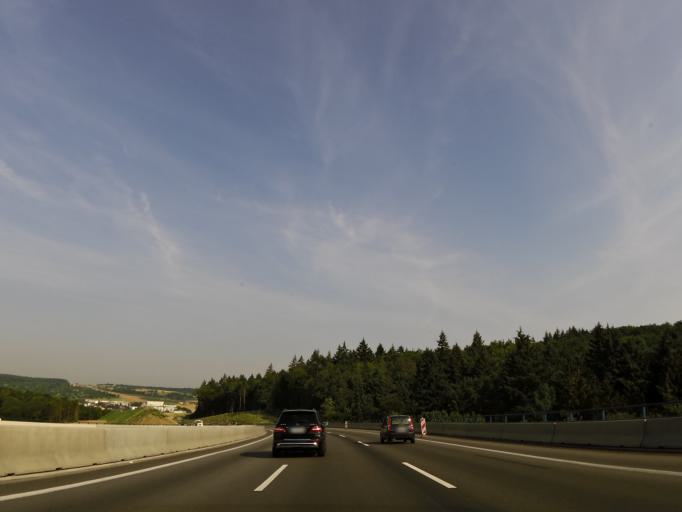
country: DE
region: Baden-Wuerttemberg
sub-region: Karlsruhe Region
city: Konigsbach-Stein
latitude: 48.9278
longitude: 8.5871
